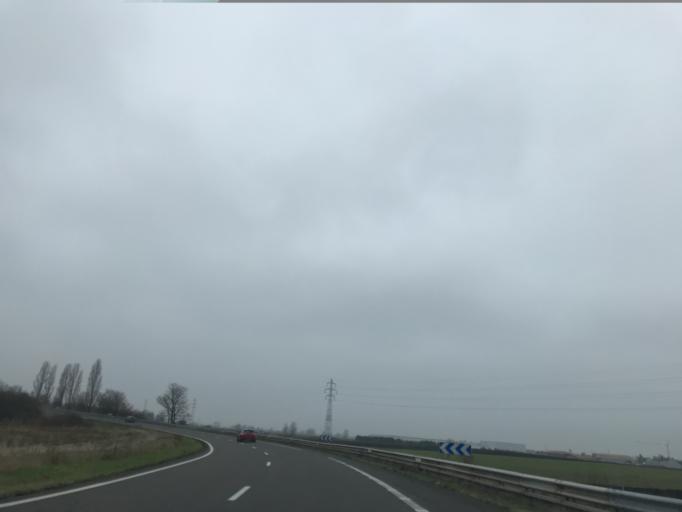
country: FR
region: Auvergne
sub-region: Departement du Puy-de-Dome
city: Pont-du-Chateau
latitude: 45.8303
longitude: 3.2271
